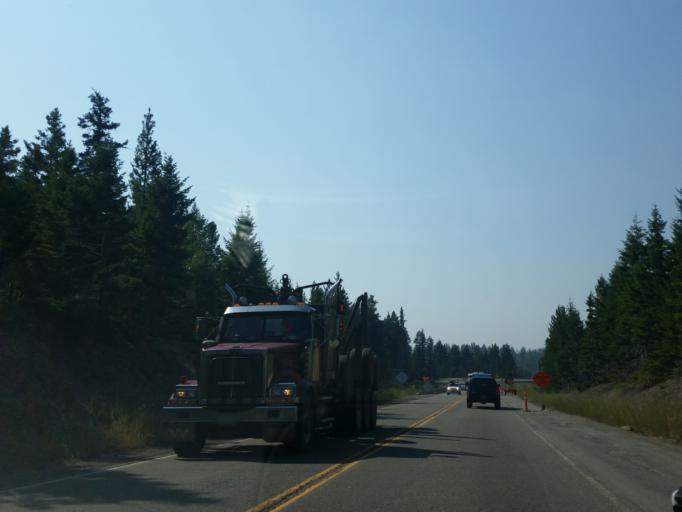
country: CA
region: British Columbia
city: Princeton
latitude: 49.2874
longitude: -120.5780
